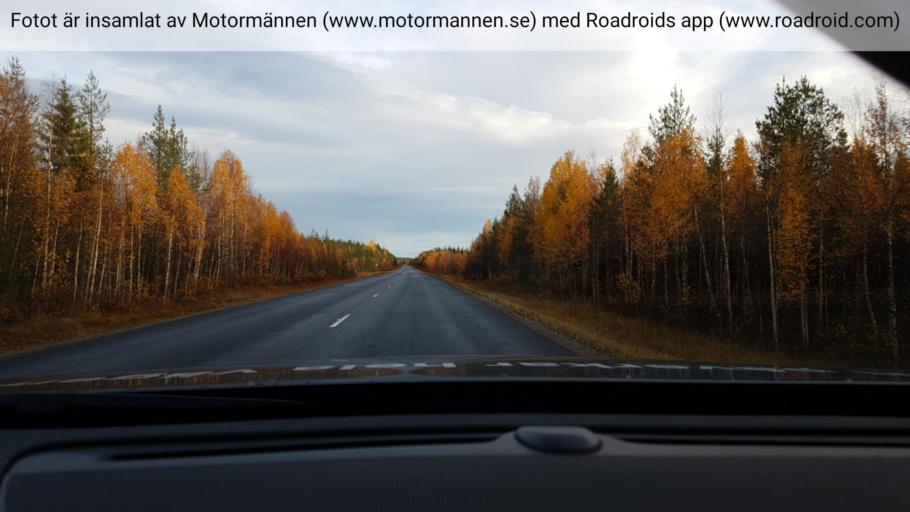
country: SE
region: Norrbotten
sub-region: Overkalix Kommun
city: OEverkalix
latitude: 67.0019
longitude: 22.5554
